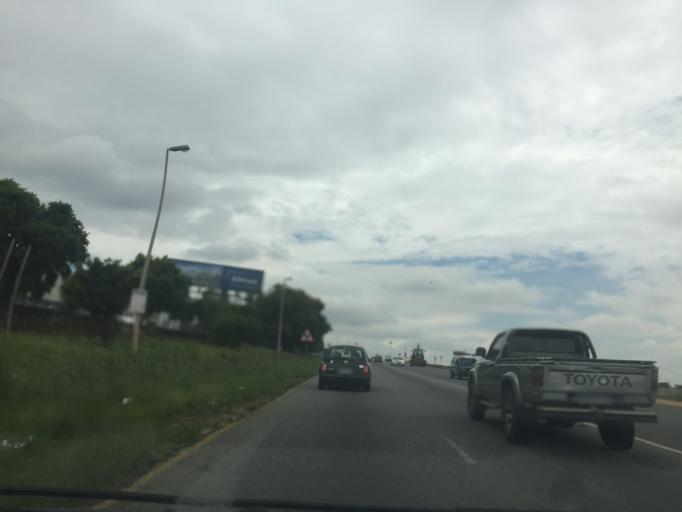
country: ZA
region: Gauteng
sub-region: City of Johannesburg Metropolitan Municipality
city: Midrand
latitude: -26.0116
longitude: 28.1309
